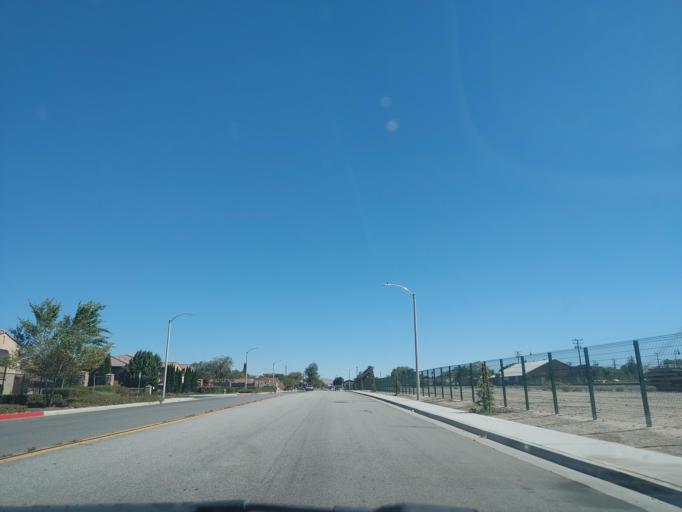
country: US
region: California
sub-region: Kern County
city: Tehachapi
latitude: 35.1335
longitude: -118.4515
